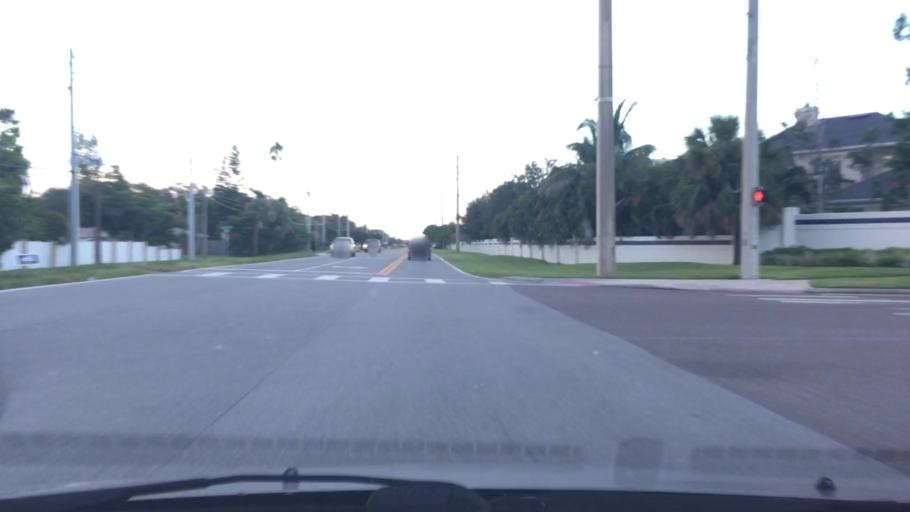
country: US
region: Florida
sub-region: Brevard County
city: Indian Harbour Beach
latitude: 28.1213
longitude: -80.5880
